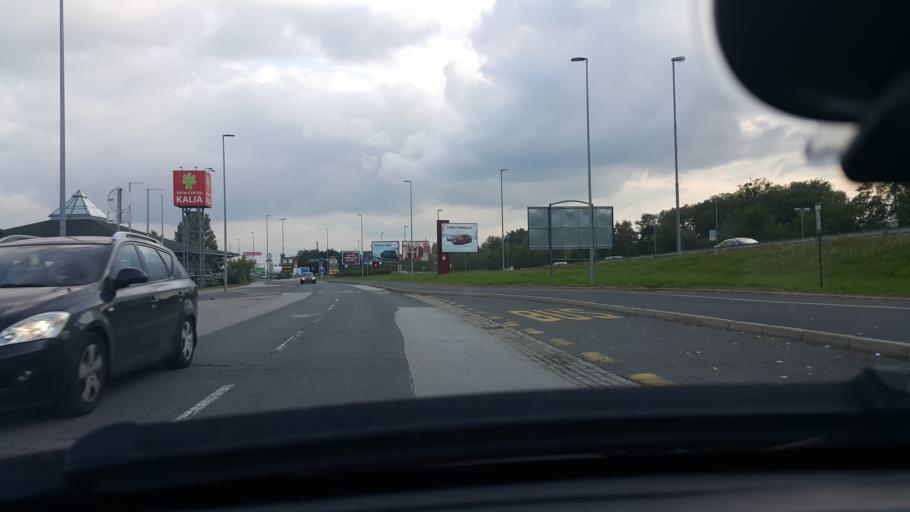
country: SI
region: Maribor
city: Razvanje
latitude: 46.5310
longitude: 15.6460
